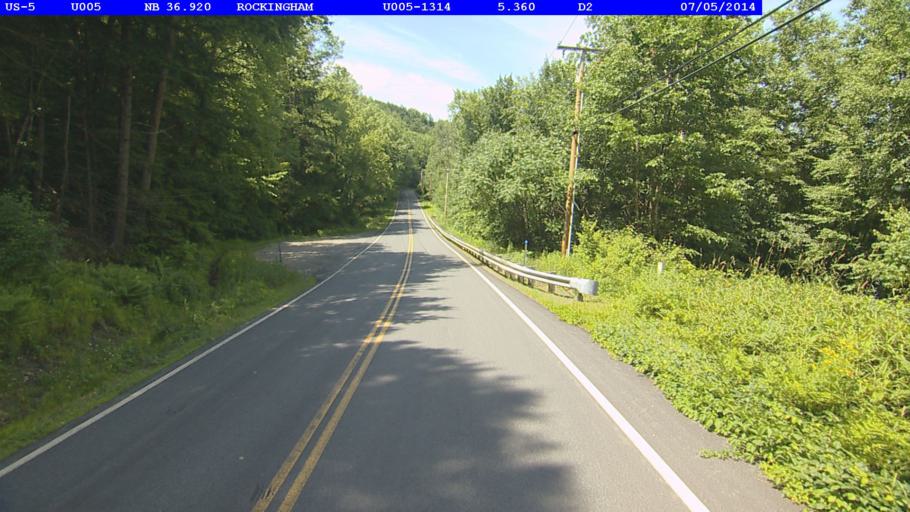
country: US
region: Vermont
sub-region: Windham County
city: Rockingham
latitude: 43.1928
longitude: -72.4511
